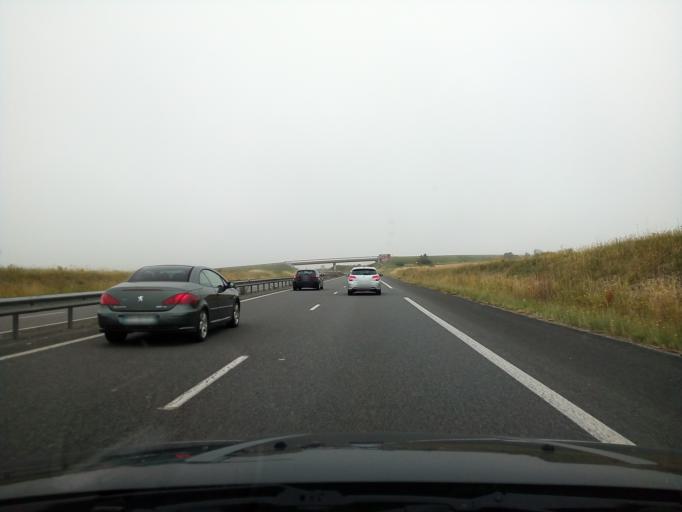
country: FR
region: Poitou-Charentes
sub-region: Departement de la Charente
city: Jarnac
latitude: 45.6976
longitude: -0.1203
